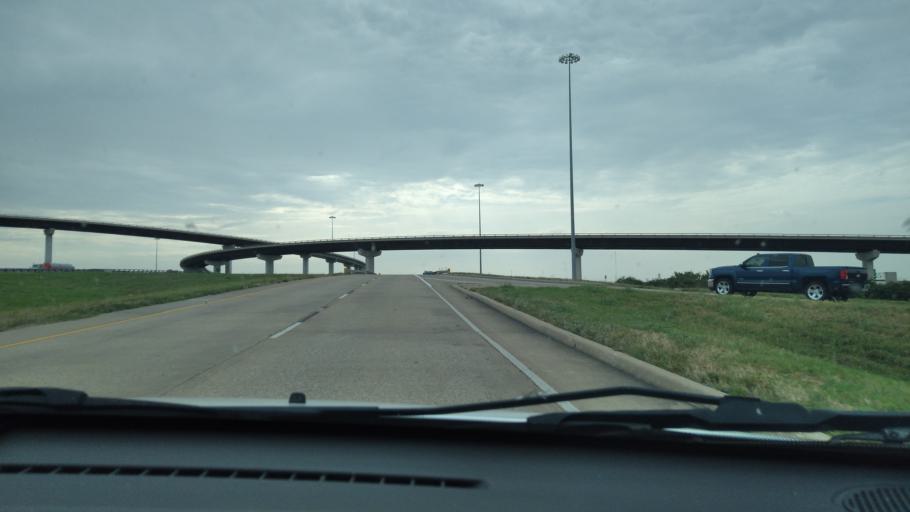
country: US
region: Texas
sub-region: McLennan County
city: Beverly Hills
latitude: 31.4930
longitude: -97.1487
